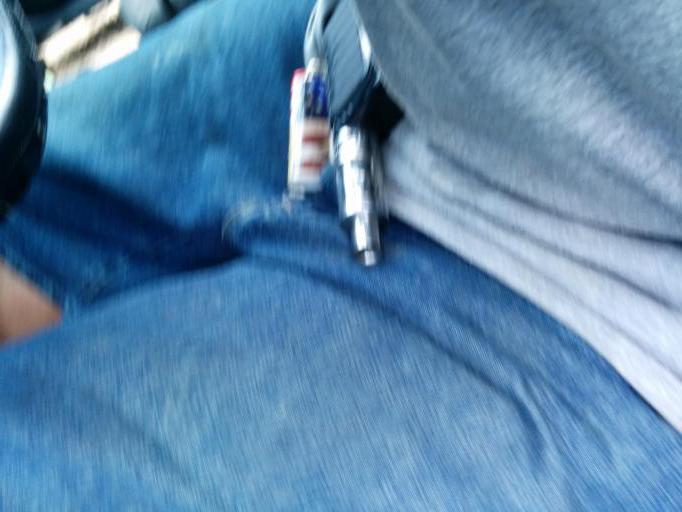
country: US
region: Oklahoma
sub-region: Tulsa County
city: Owasso
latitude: 36.1732
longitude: -95.8867
